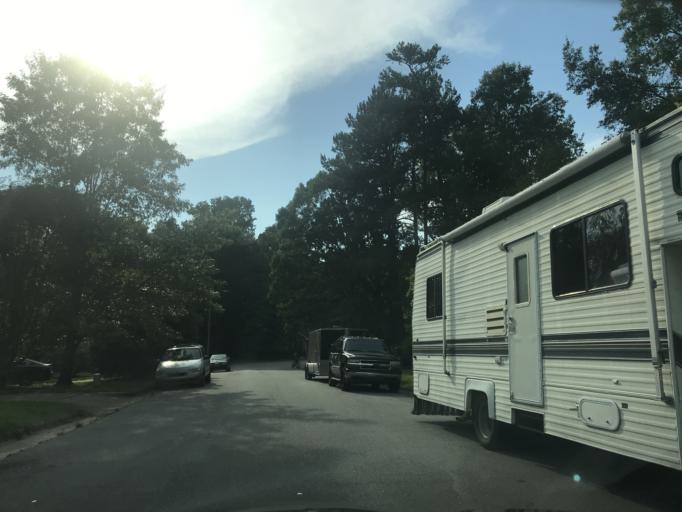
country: US
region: North Carolina
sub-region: Wake County
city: Raleigh
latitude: 35.8299
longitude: -78.5891
